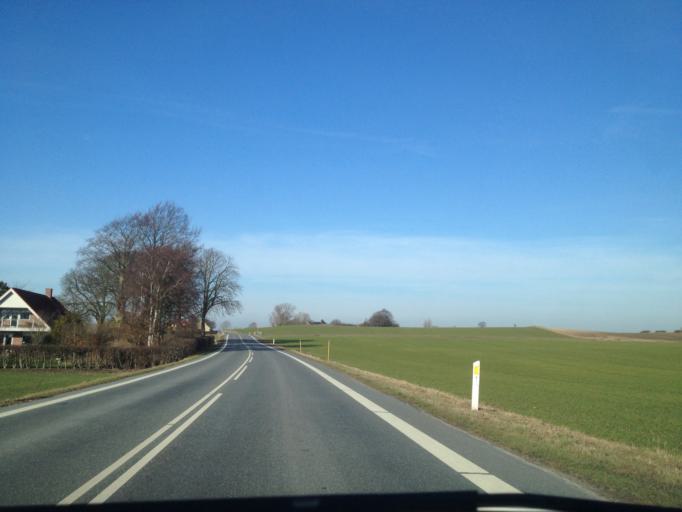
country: DK
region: South Denmark
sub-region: Kerteminde Kommune
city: Kerteminde
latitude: 55.4789
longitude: 10.6632
